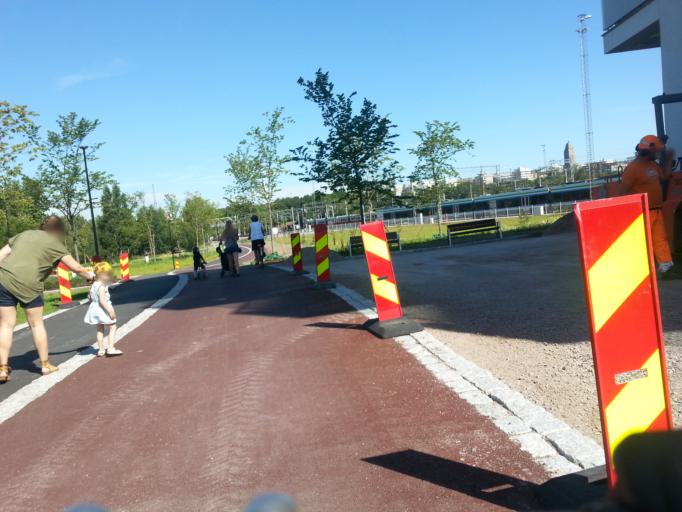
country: FI
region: Uusimaa
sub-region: Helsinki
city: Helsinki
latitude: 60.1771
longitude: 24.9381
